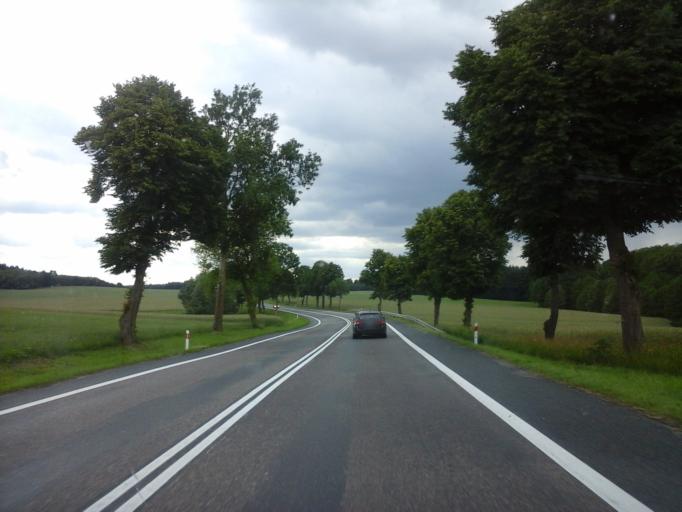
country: PL
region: West Pomeranian Voivodeship
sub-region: Powiat bialogardzki
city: Karlino
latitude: 54.0039
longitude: 15.7825
